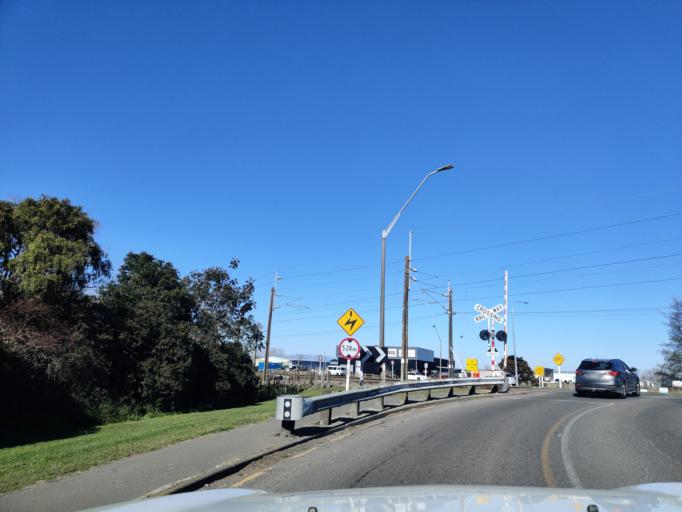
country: NZ
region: Manawatu-Wanganui
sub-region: Palmerston North City
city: Palmerston North
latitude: -40.2322
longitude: 175.5740
